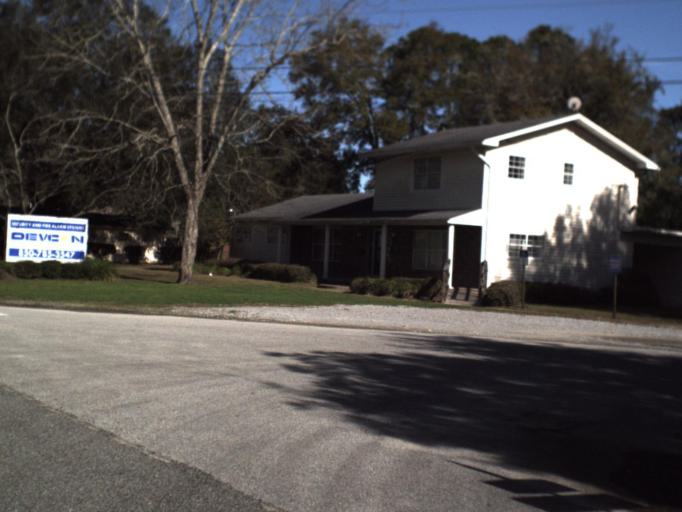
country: US
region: Florida
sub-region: Bay County
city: Pretty Bayou
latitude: 30.1860
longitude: -85.6718
